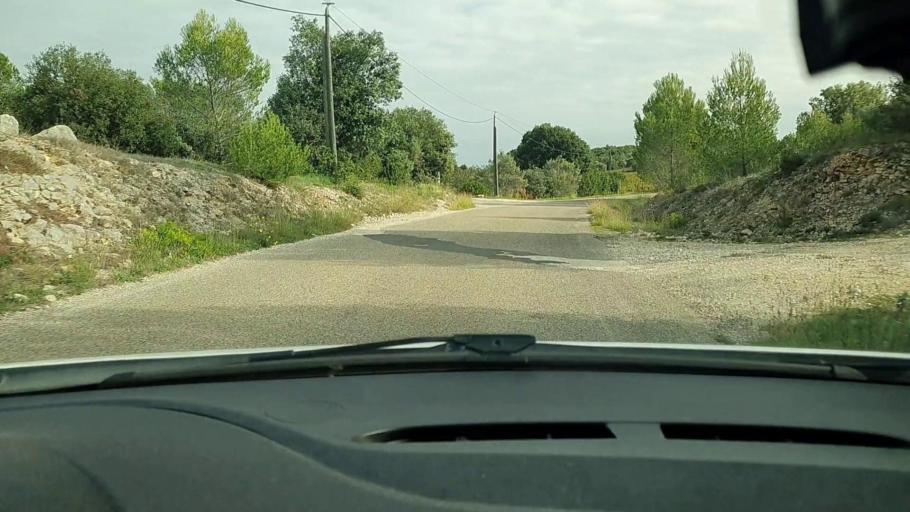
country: FR
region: Languedoc-Roussillon
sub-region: Departement du Gard
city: Montaren-et-Saint-Mediers
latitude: 44.0840
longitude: 4.3874
